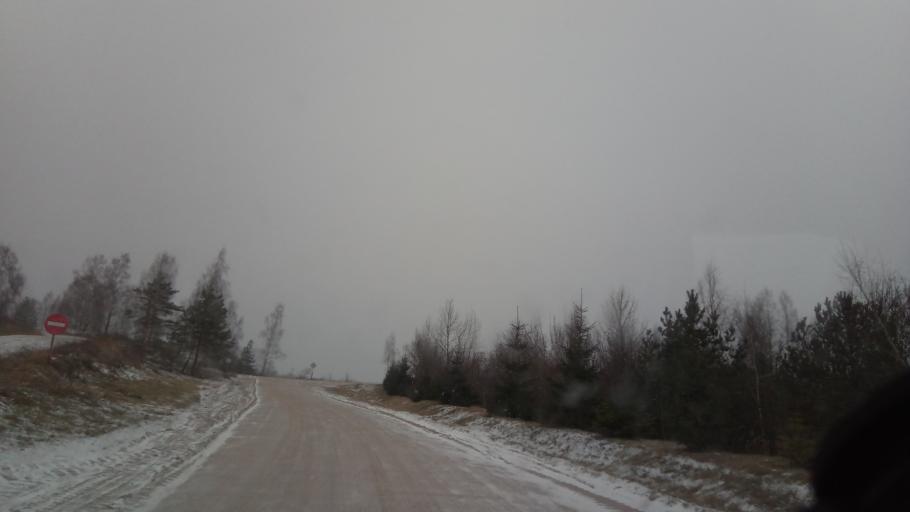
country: LT
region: Vilnius County
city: Ukmerge
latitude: 55.3316
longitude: 24.8825
